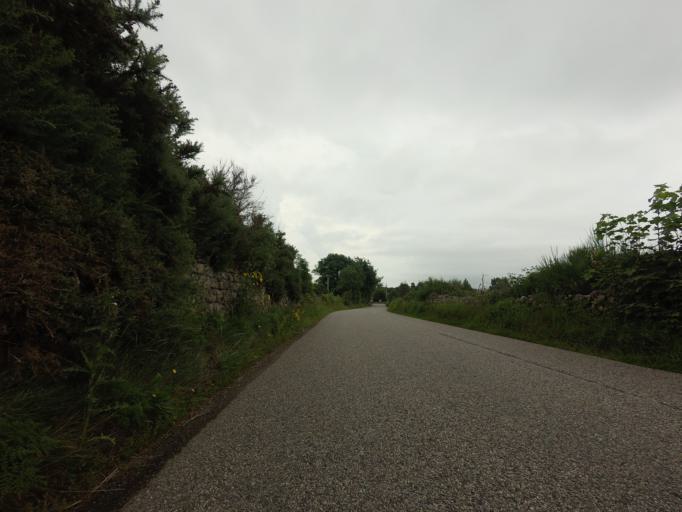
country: GB
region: Scotland
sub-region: Highland
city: Evanton
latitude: 57.8859
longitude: -4.3812
